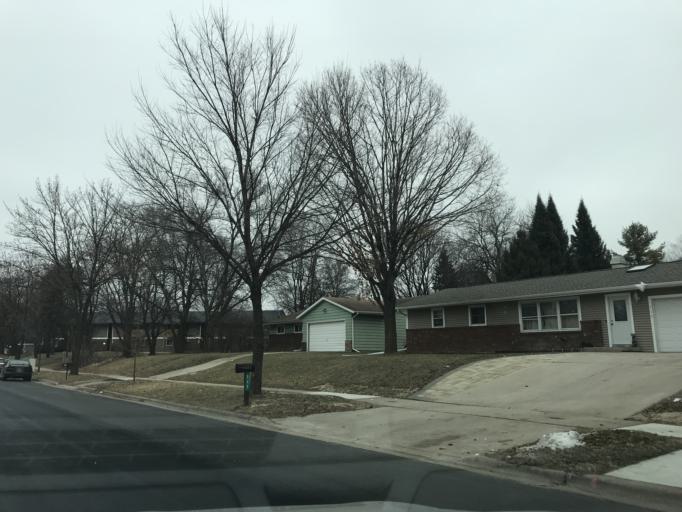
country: US
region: Wisconsin
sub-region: Dane County
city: Monona
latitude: 43.1016
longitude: -89.3016
